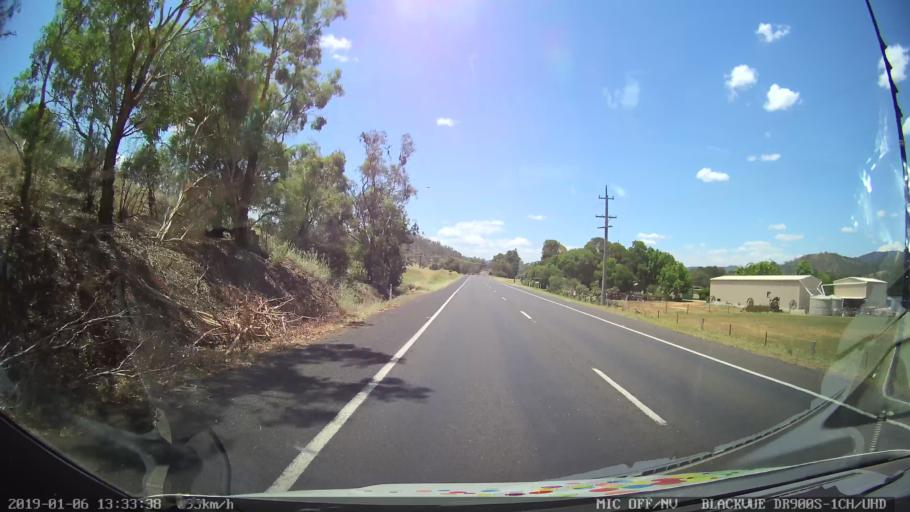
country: AU
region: New South Wales
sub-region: Tamworth Municipality
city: Kootingal
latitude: -31.0969
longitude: 151.0081
